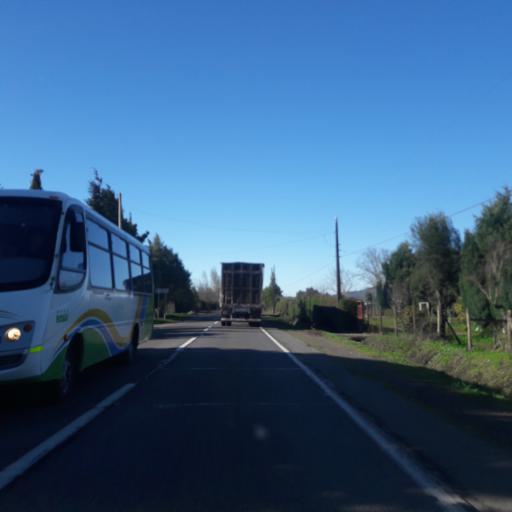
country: CL
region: Araucania
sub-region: Provincia de Malleco
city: Angol
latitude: -37.7774
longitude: -72.5399
